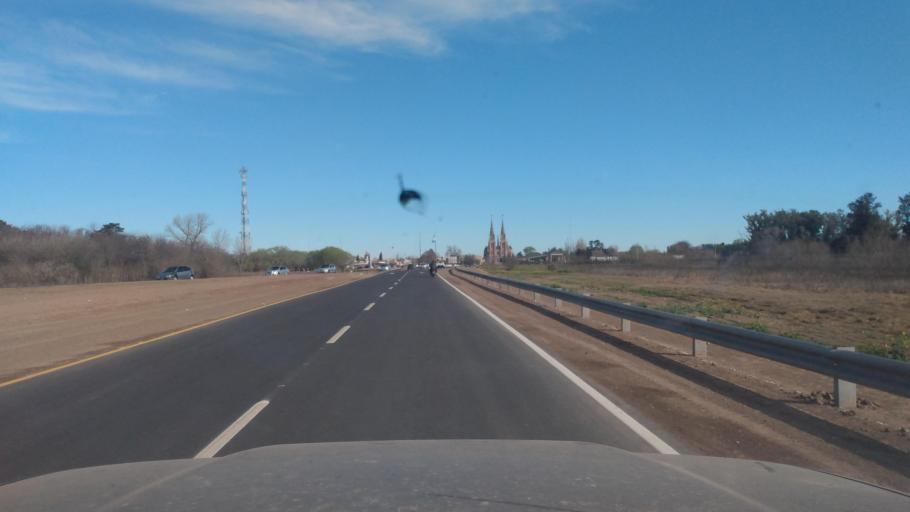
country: AR
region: Buenos Aires
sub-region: Partido de Lujan
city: Lujan
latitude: -34.5511
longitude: -59.1161
